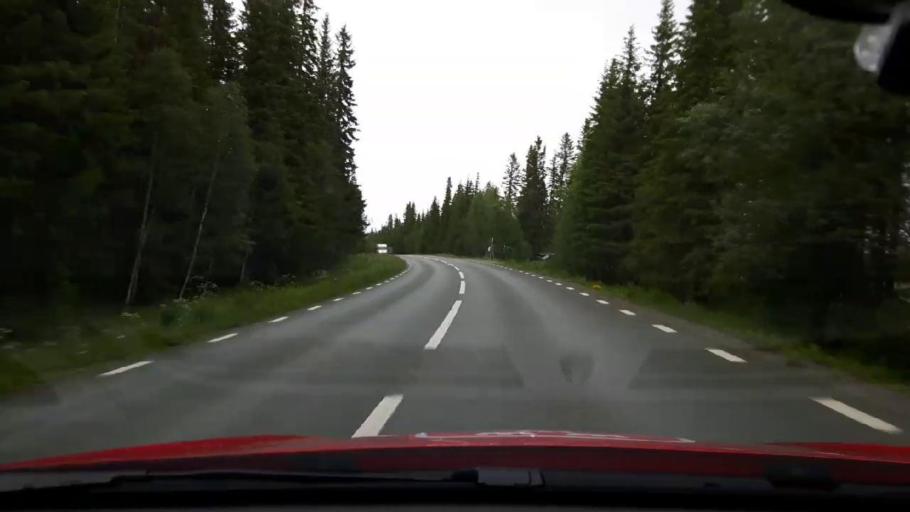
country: SE
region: Jaemtland
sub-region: Are Kommun
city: Are
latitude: 63.3474
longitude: 12.5873
